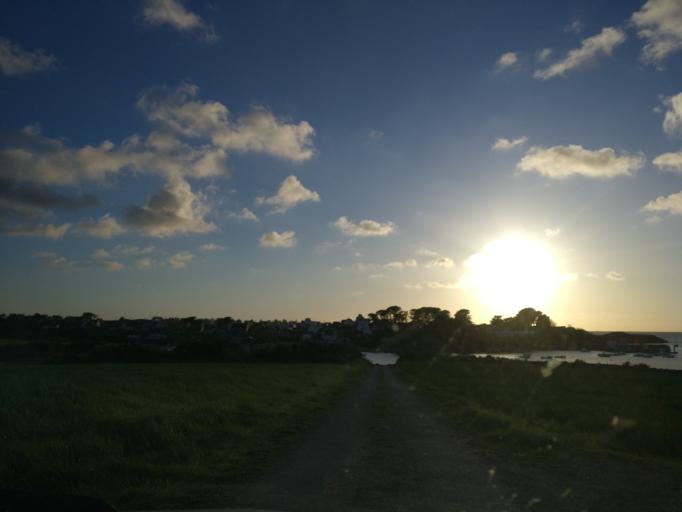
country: FR
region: Brittany
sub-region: Departement du Finistere
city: Lampaul-Plouarzel
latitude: 48.4669
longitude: -4.7519
